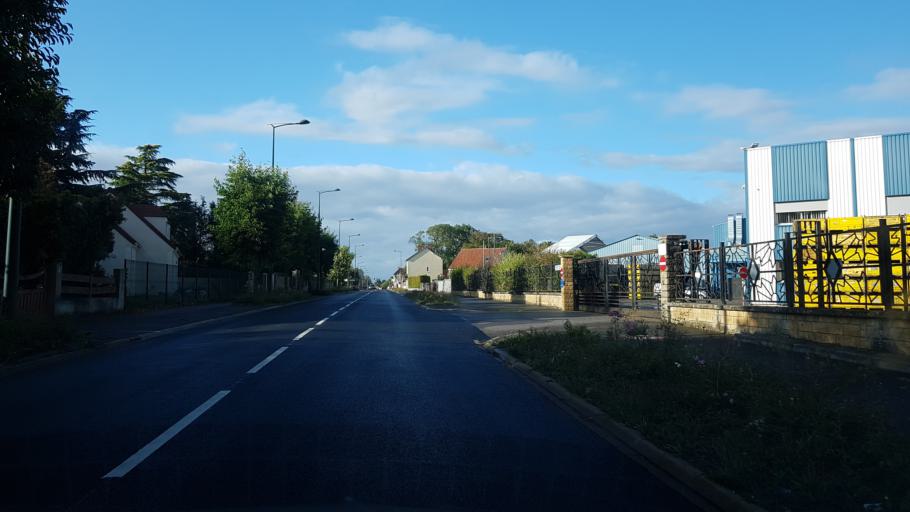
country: FR
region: Centre
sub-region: Departement du Loiret
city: Sermaises
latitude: 48.2921
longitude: 2.2031
